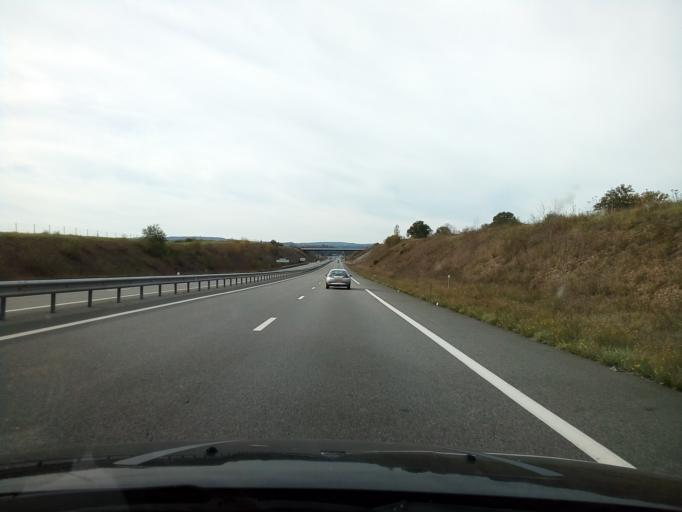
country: FR
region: Limousin
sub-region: Departement de la Creuse
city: Gouzon
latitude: 46.1944
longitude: 2.1669
